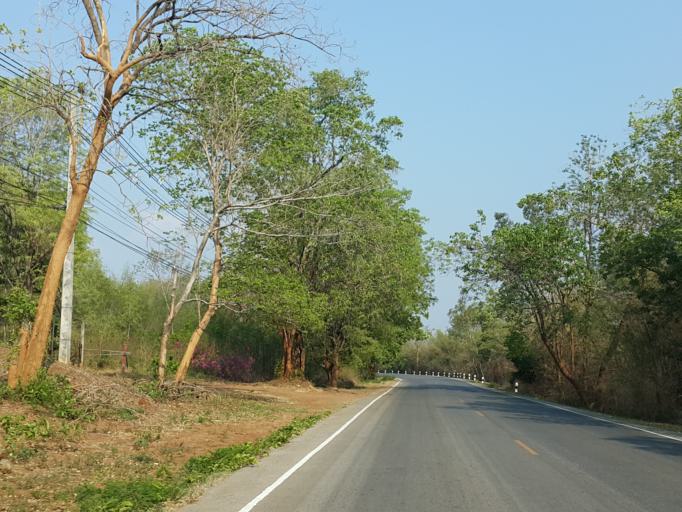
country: TH
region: Kanchanaburi
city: Sai Yok
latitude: 14.2195
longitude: 99.1759
